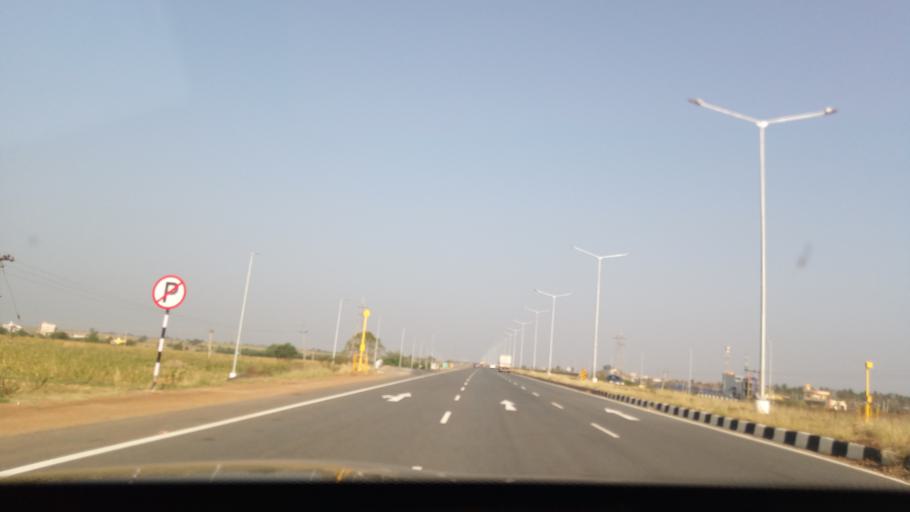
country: IN
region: Karnataka
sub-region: Haveri
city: Ranibennur
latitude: 14.5993
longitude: 75.6276
